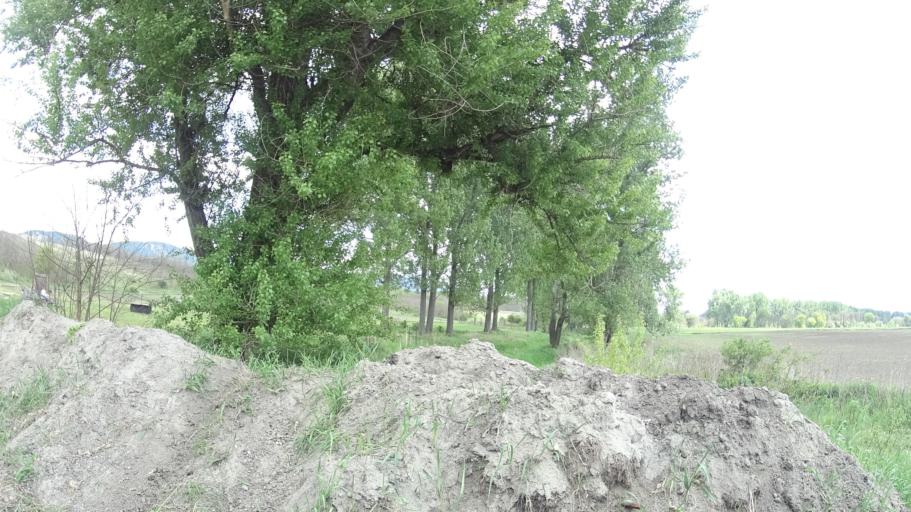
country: HU
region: Komarom-Esztergom
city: Dorog
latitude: 47.7171
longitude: 18.7505
